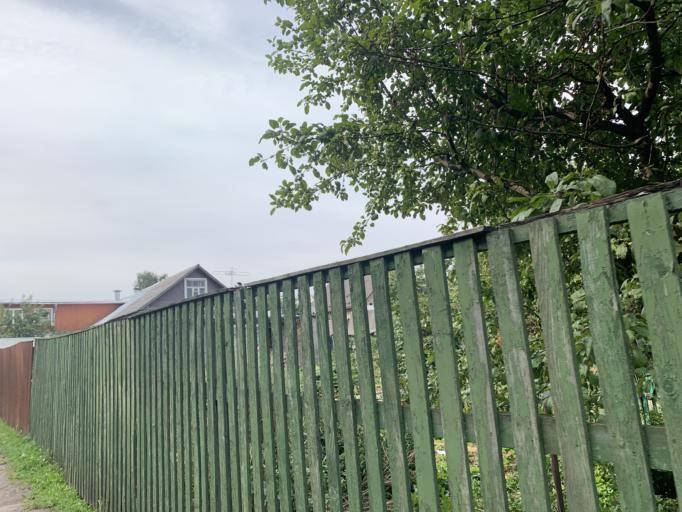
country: RU
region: Moskovskaya
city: Cherkizovo
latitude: 55.9421
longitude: 37.7930
